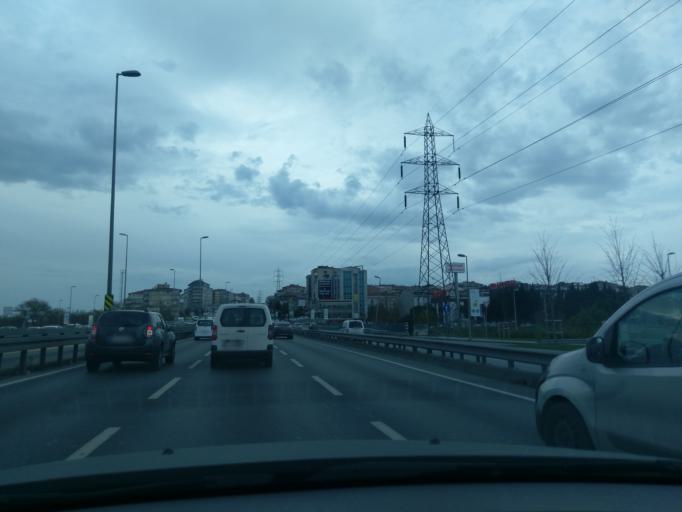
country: TR
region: Istanbul
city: Yakuplu
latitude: 40.9798
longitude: 28.7501
